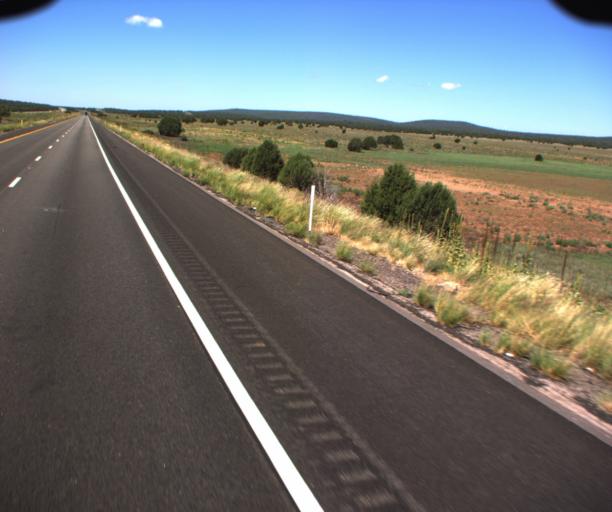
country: US
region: Arizona
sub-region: Mohave County
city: Peach Springs
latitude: 35.2336
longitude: -113.2146
